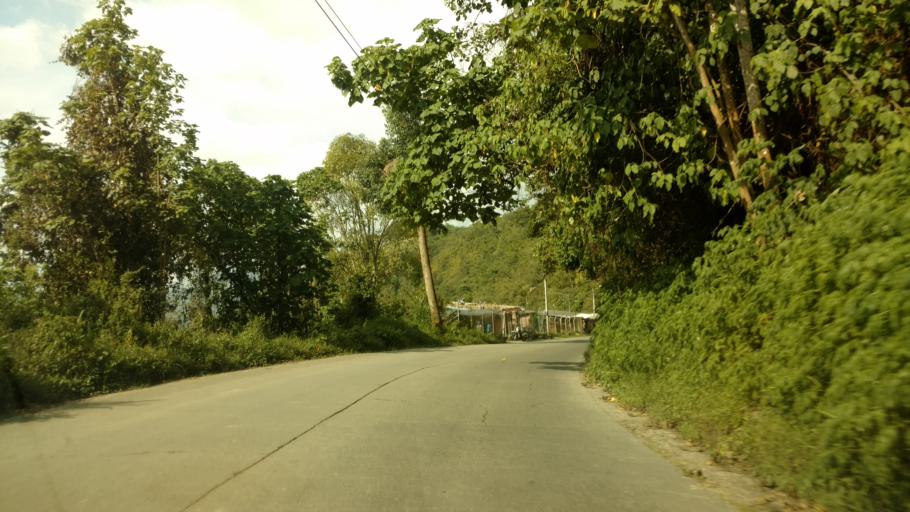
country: CO
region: Caldas
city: Manizales
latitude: 5.0895
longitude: -75.5165
